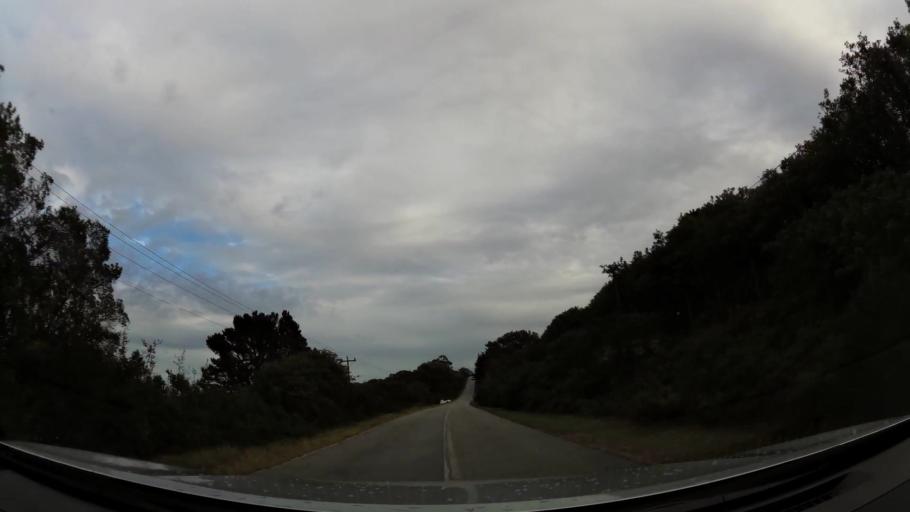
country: ZA
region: Eastern Cape
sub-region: Nelson Mandela Bay Metropolitan Municipality
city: Port Elizabeth
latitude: -34.0074
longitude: 25.4837
